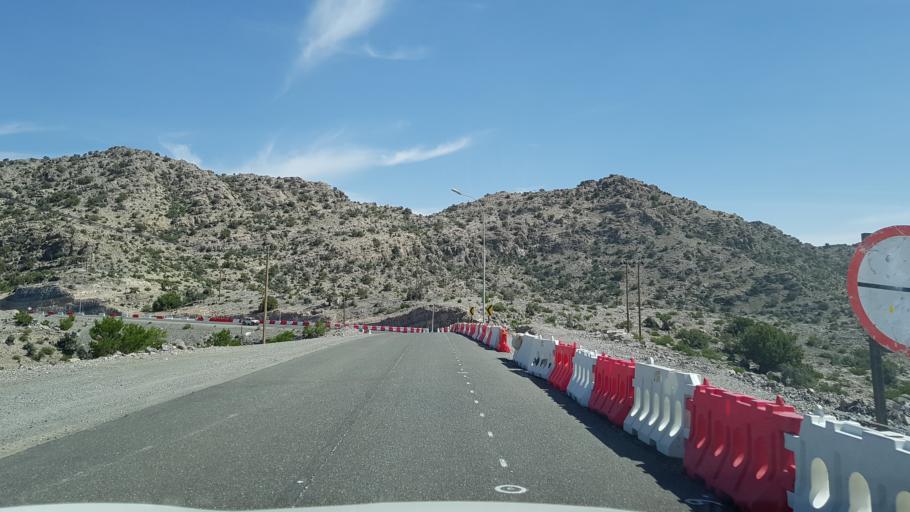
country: OM
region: Muhafazat ad Dakhiliyah
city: Nizwa
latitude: 23.1150
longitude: 57.6472
